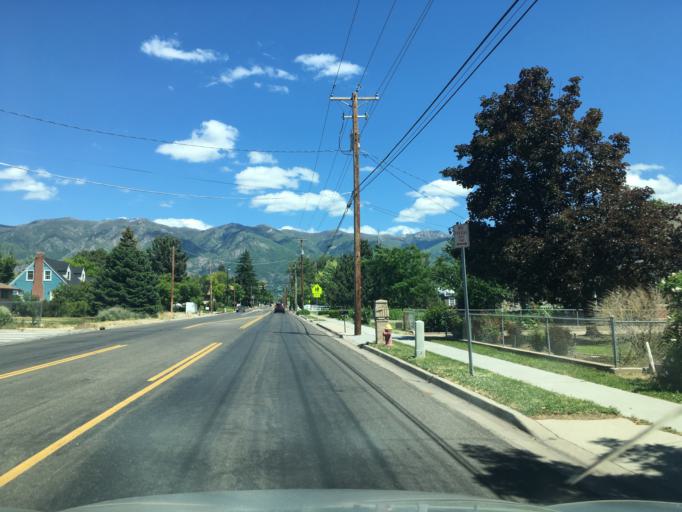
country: US
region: Utah
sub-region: Davis County
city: Layton
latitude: 41.0601
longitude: -111.9775
